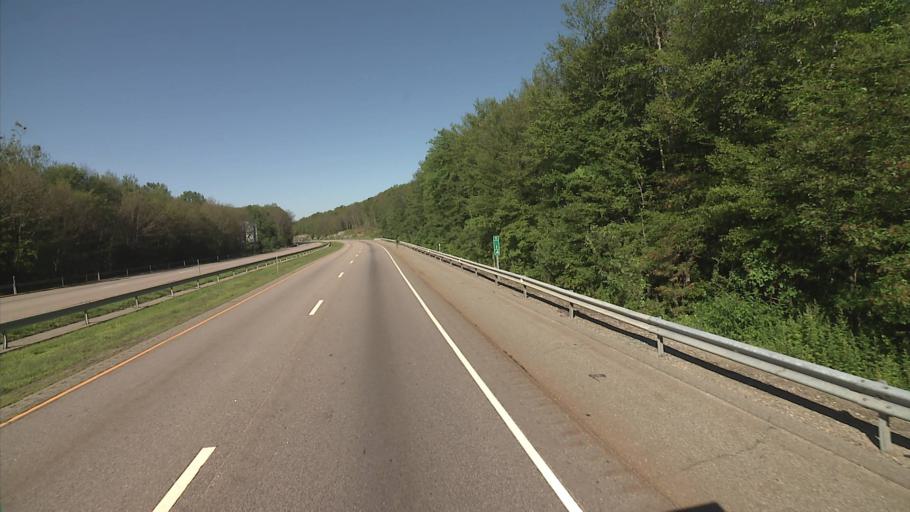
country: US
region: Connecticut
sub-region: New London County
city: Central Waterford
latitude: 41.3915
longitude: -72.1758
